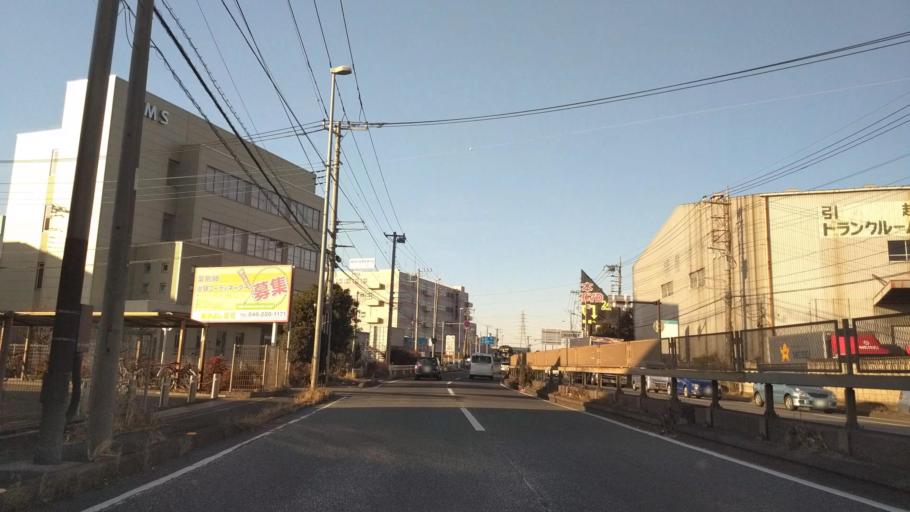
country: JP
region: Kanagawa
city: Atsugi
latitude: 35.4279
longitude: 139.3570
